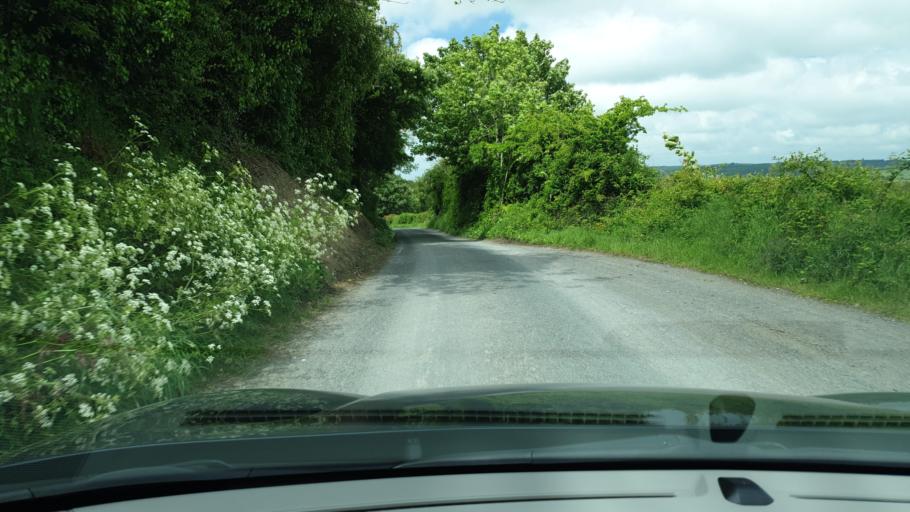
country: IE
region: Leinster
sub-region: An Mhi
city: Slane
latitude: 53.7325
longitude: -6.5523
